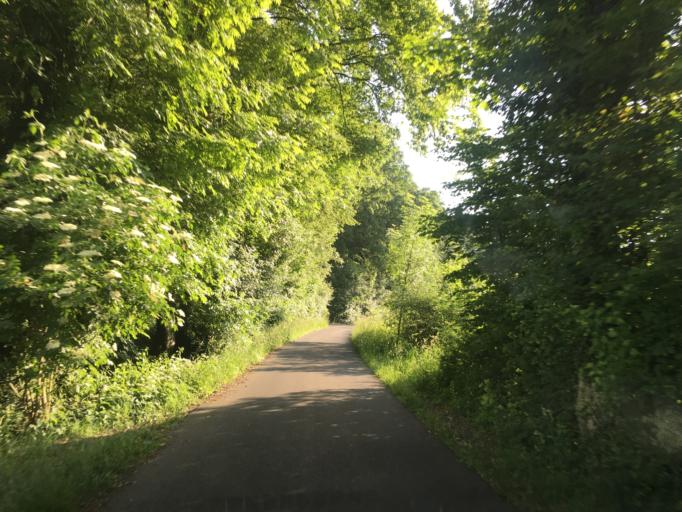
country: DE
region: North Rhine-Westphalia
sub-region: Regierungsbezirk Munster
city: Muenster
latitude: 52.0068
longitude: 7.5642
